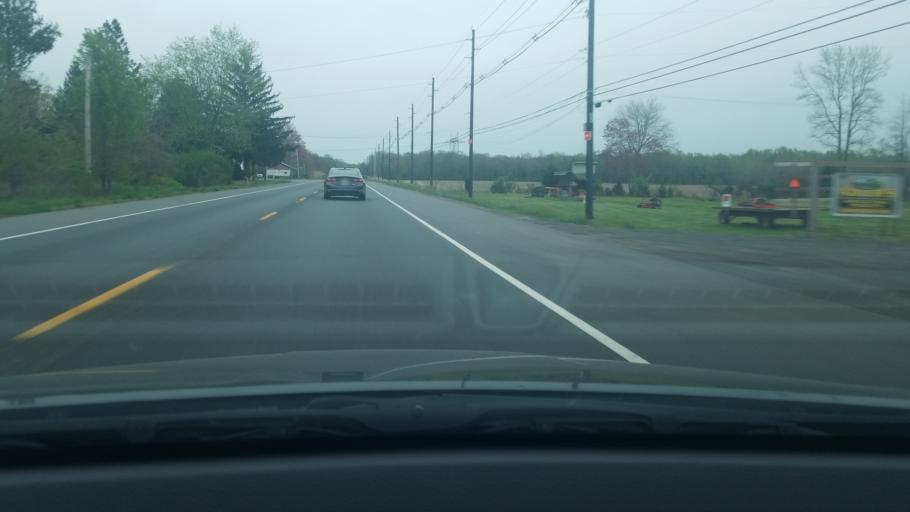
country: US
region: New Jersey
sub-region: Burlington County
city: Medford Lakes
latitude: 39.8941
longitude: -74.7744
